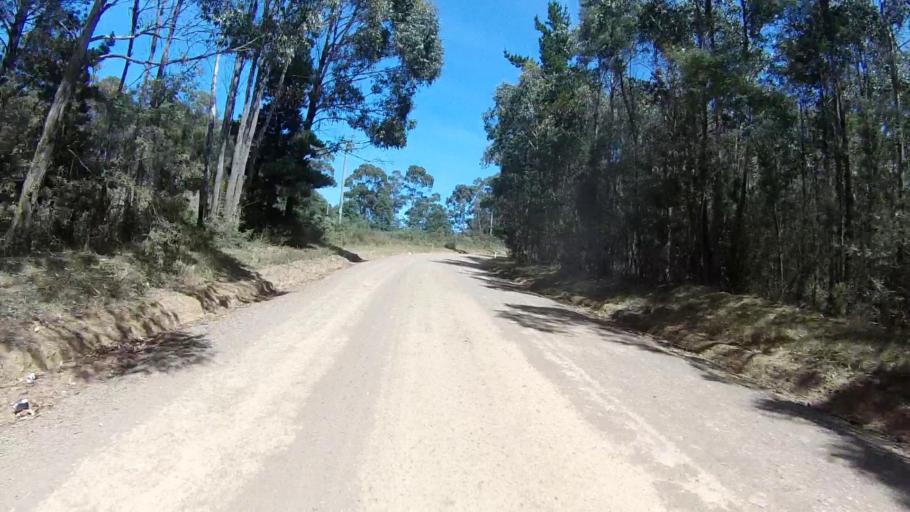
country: AU
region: Tasmania
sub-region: Sorell
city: Sorell
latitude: -42.7527
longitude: 147.6955
